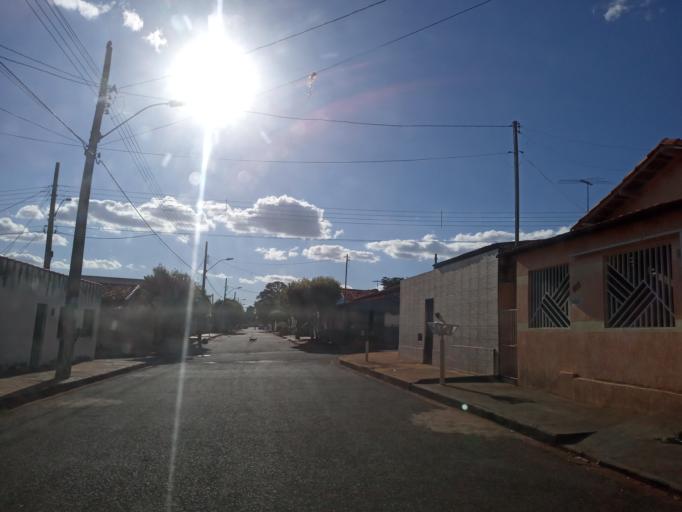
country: BR
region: Minas Gerais
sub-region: Ituiutaba
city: Ituiutaba
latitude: -18.9747
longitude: -49.4473
